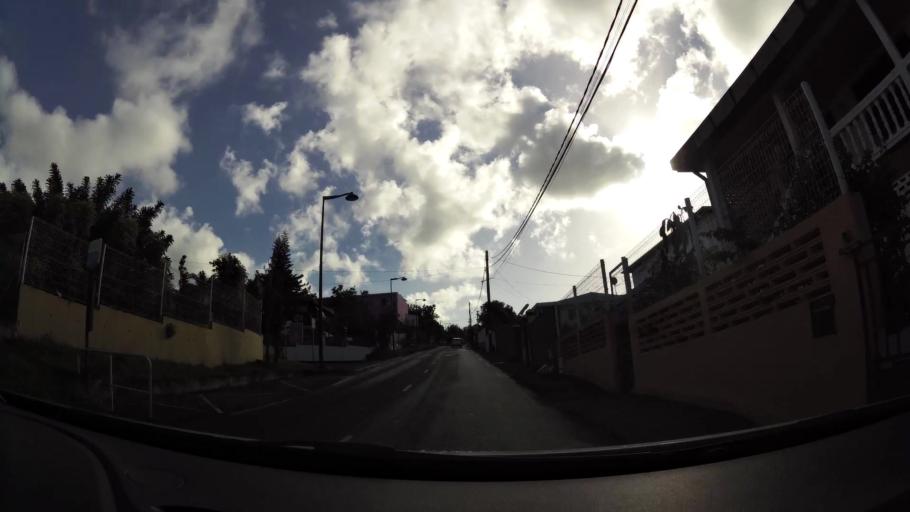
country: MQ
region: Martinique
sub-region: Martinique
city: Le Lamentin
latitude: 14.6218
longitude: -61.0219
